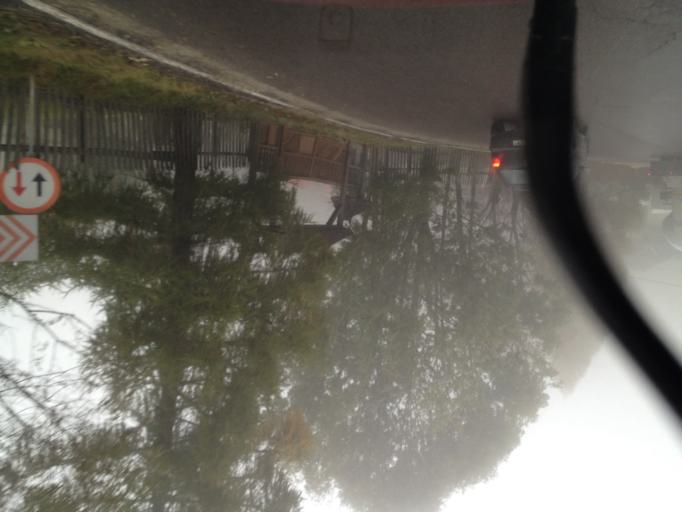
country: RO
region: Arges
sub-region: Comuna Dambovicioara
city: Dambovicioara
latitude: 45.4268
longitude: 25.2490
